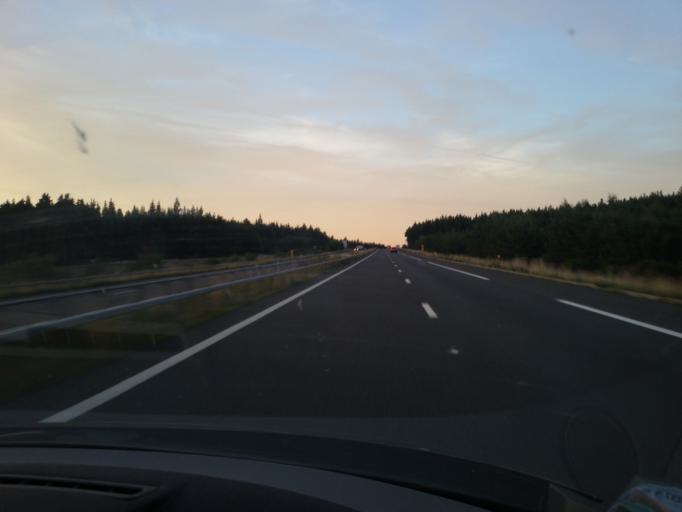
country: FR
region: Languedoc-Roussillon
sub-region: Departement de la Lozere
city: Aumont-Aubrac
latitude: 44.7673
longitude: 3.2833
